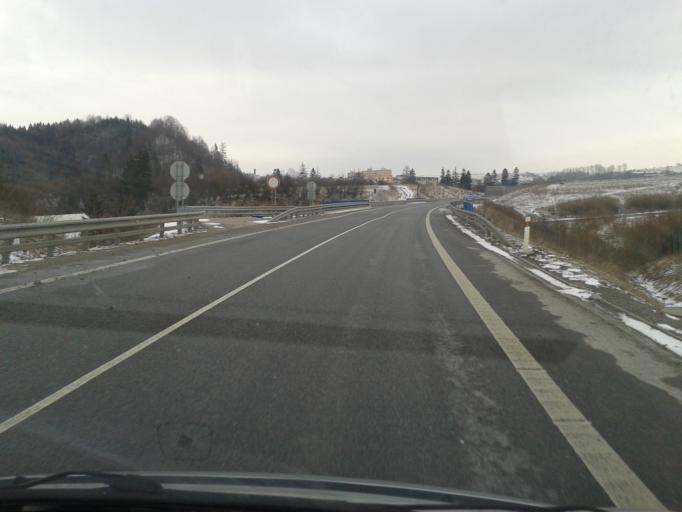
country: SK
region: Zilinsky
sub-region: Okres Zilina
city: Trstena
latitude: 49.3499
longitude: 19.5856
